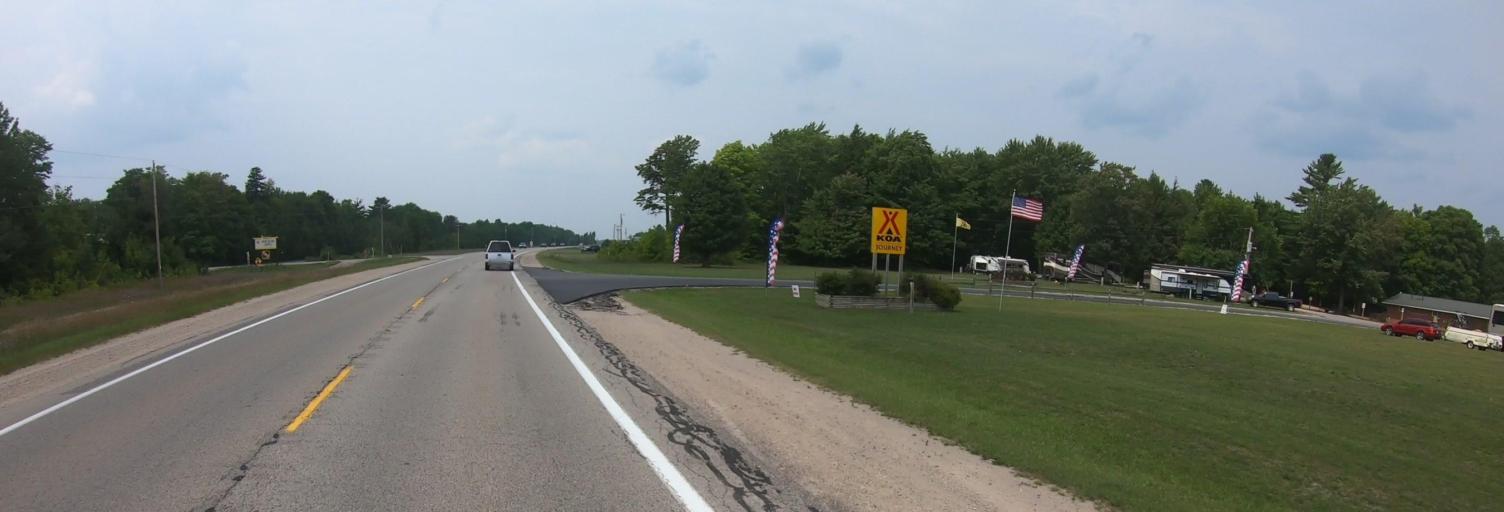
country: US
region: Michigan
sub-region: Alger County
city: Munising
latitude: 46.3772
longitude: -86.5933
